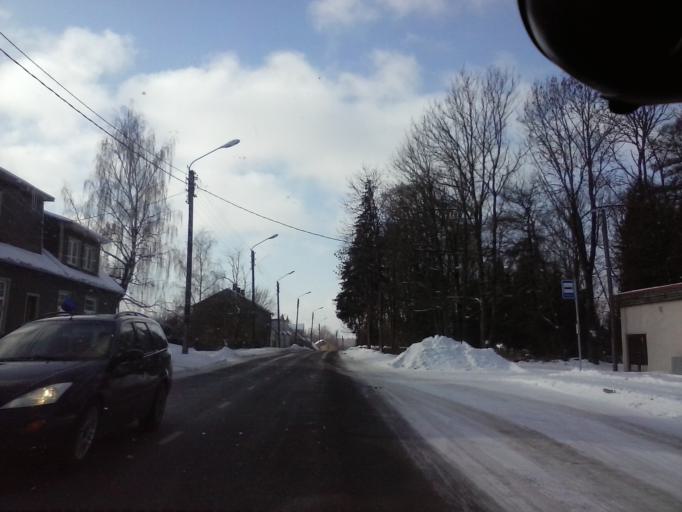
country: EE
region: Viljandimaa
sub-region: Viljandi linn
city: Viljandi
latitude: 58.3590
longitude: 25.5717
